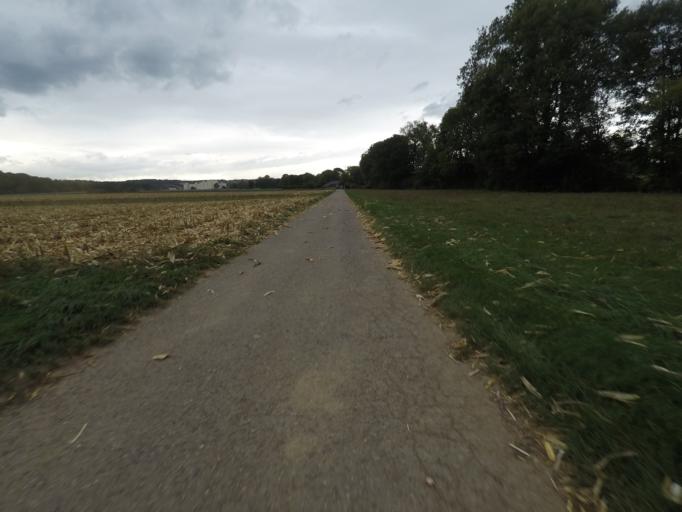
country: DE
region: Baden-Wuerttemberg
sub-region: Regierungsbezirk Stuttgart
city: Leinfelden-Echterdingen
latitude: 48.7168
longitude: 9.1367
